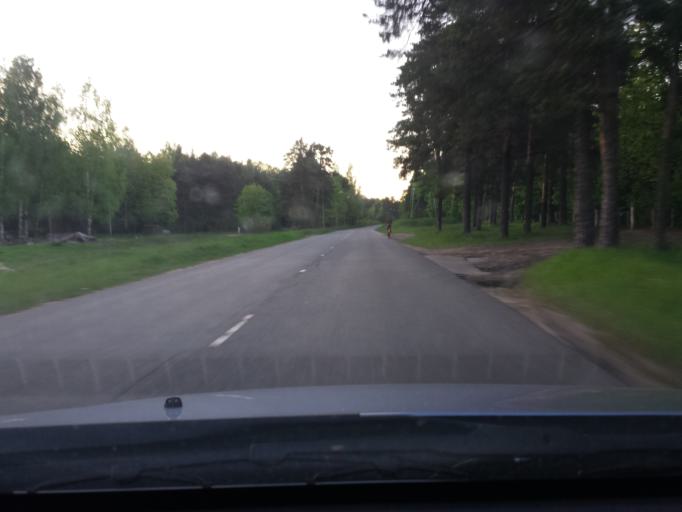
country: LV
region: Riga
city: Riga
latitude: 56.9897
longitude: 24.1410
